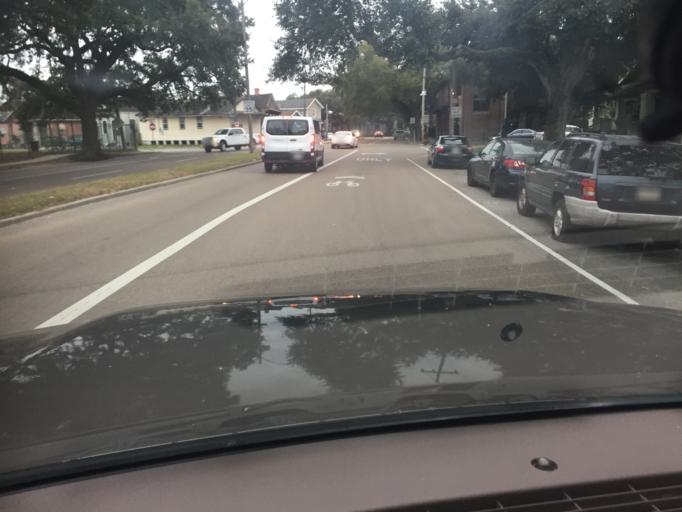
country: US
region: Louisiana
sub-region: Orleans Parish
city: New Orleans
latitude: 29.9801
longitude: -90.0776
